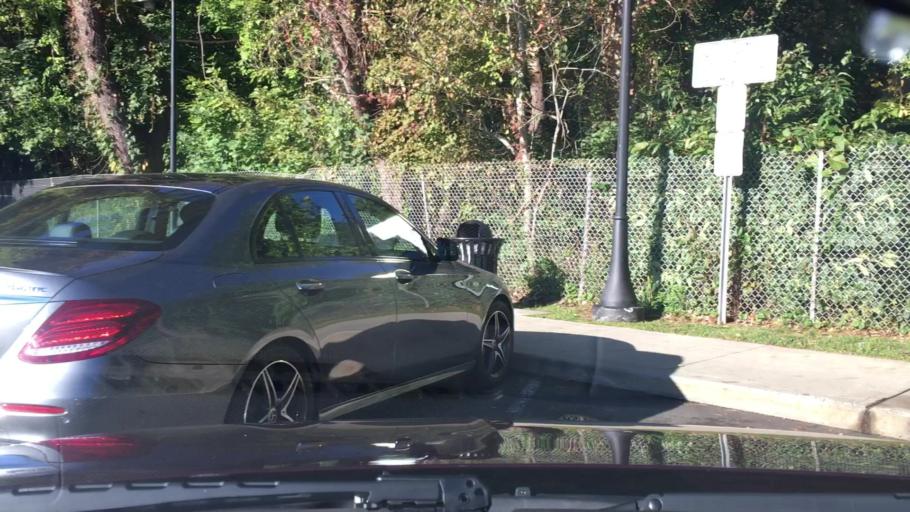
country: US
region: Connecticut
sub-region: New Haven County
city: North Haven
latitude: 41.3981
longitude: -72.8700
